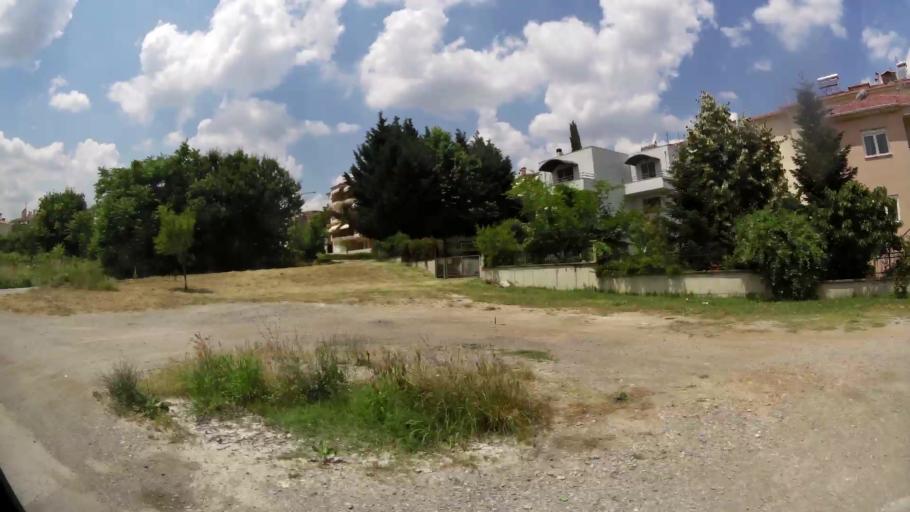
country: GR
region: West Macedonia
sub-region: Nomos Kozanis
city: Kozani
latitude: 40.2894
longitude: 21.7837
